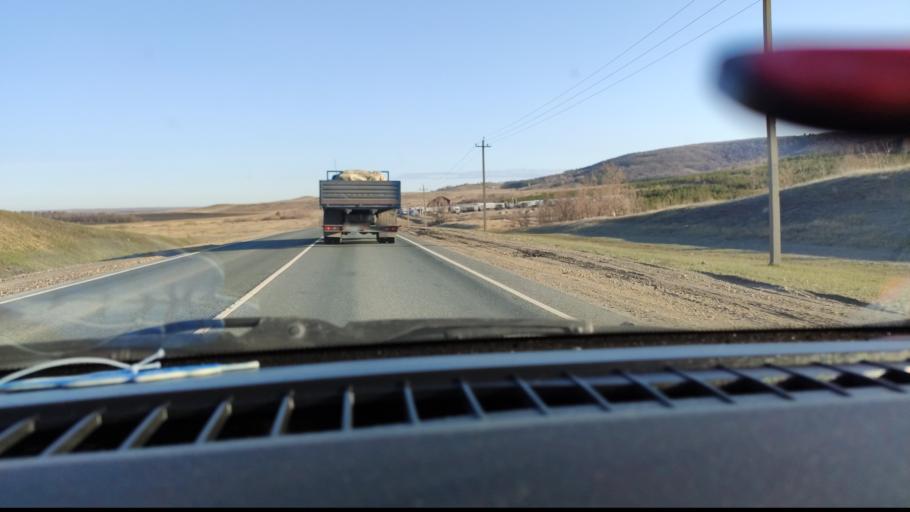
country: RU
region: Saratov
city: Alekseyevka
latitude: 52.3046
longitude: 47.9262
